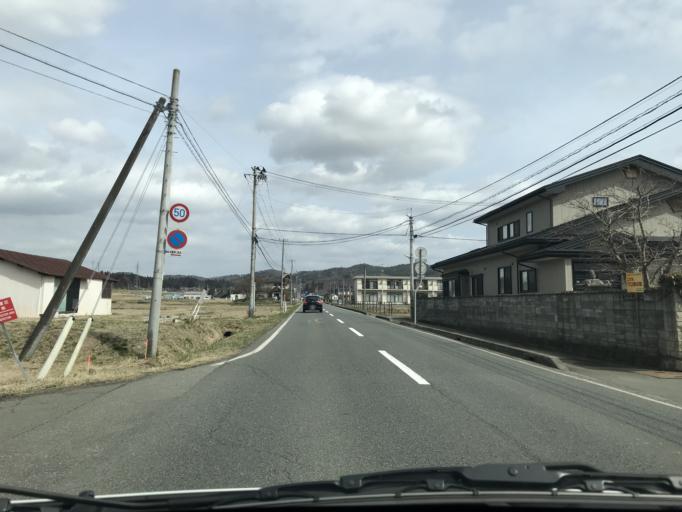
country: JP
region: Iwate
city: Mizusawa
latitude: 39.1997
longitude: 141.1868
